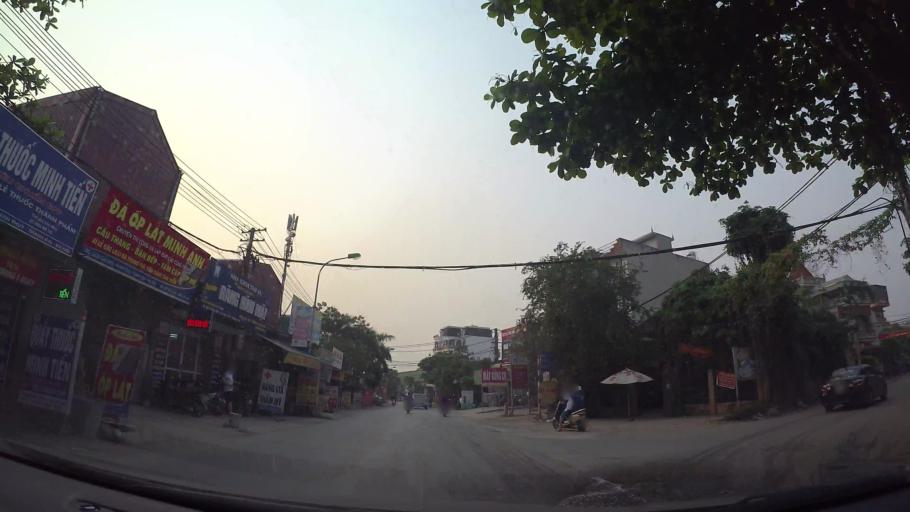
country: VN
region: Ha Noi
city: Kim Bai
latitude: 20.8710
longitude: 105.8054
